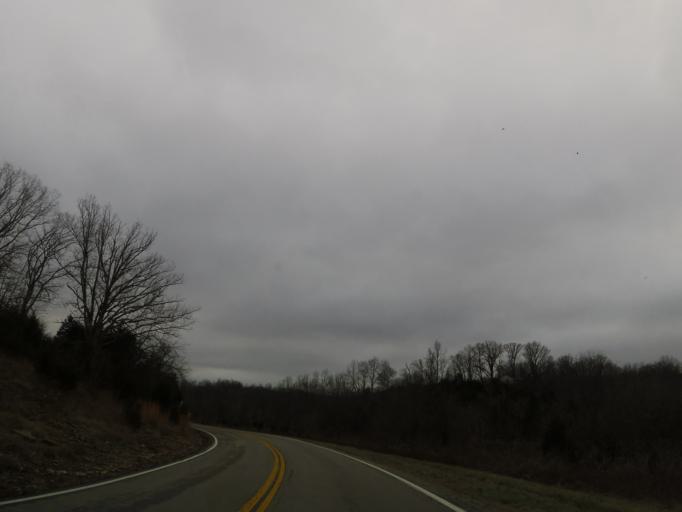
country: US
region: Kentucky
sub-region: Franklin County
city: Frankfort
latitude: 38.2934
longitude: -84.9473
